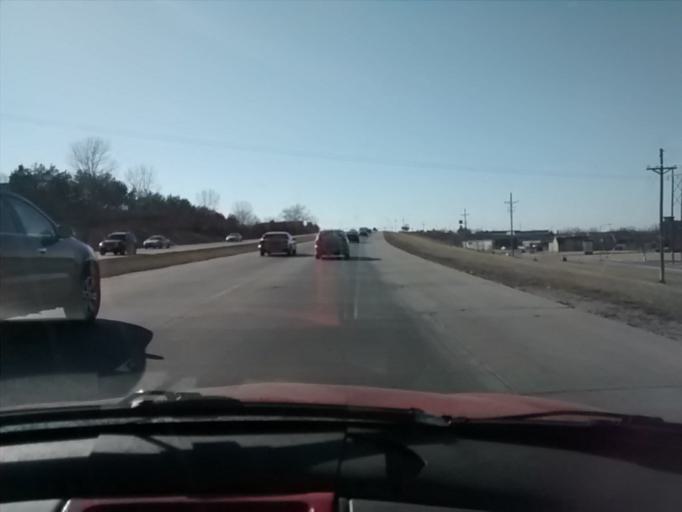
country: US
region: Nebraska
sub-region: Sarpy County
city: Offutt Air Force Base
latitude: 41.1380
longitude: -95.9604
